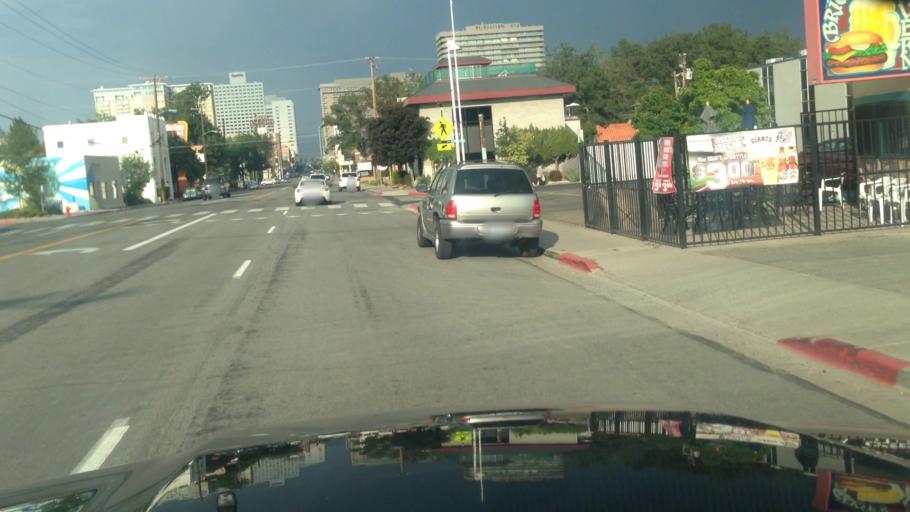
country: US
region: Nevada
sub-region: Washoe County
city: Reno
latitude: 39.5250
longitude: -119.8231
